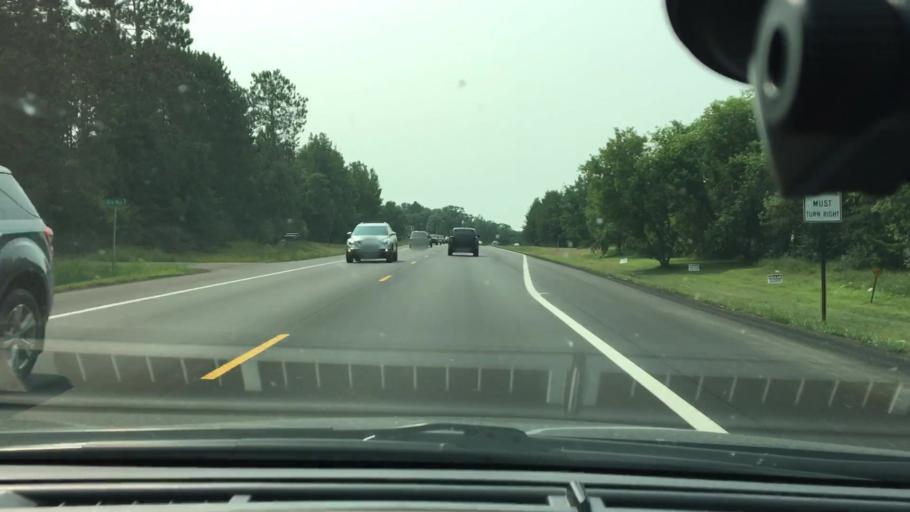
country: US
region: Minnesota
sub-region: Crow Wing County
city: Brainerd
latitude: 46.4396
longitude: -94.1716
